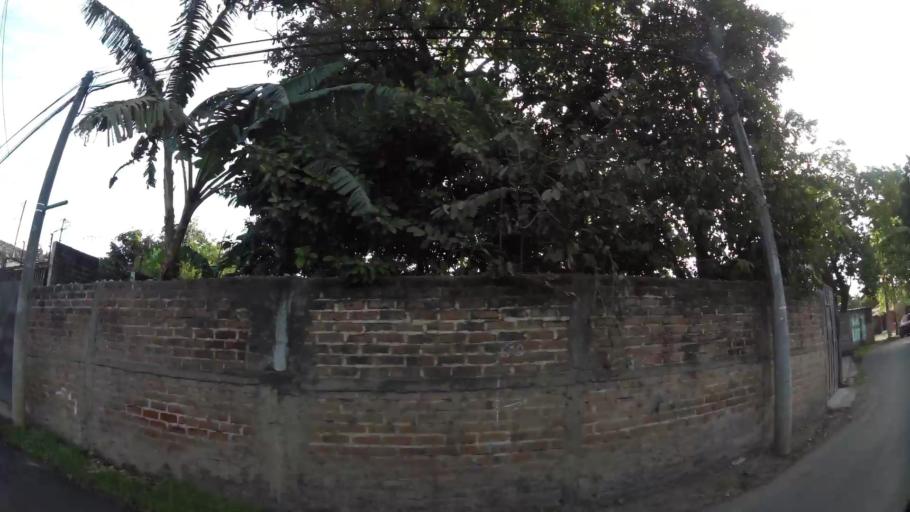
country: SV
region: Santa Ana
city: Santa Ana
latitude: 14.0013
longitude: -89.5649
